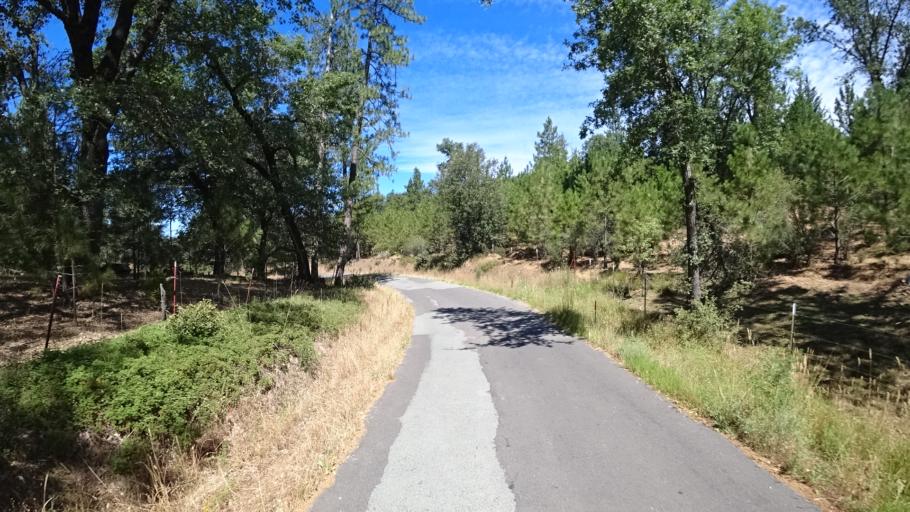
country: US
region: California
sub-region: Calaveras County
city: Mountain Ranch
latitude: 38.3375
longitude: -120.4948
